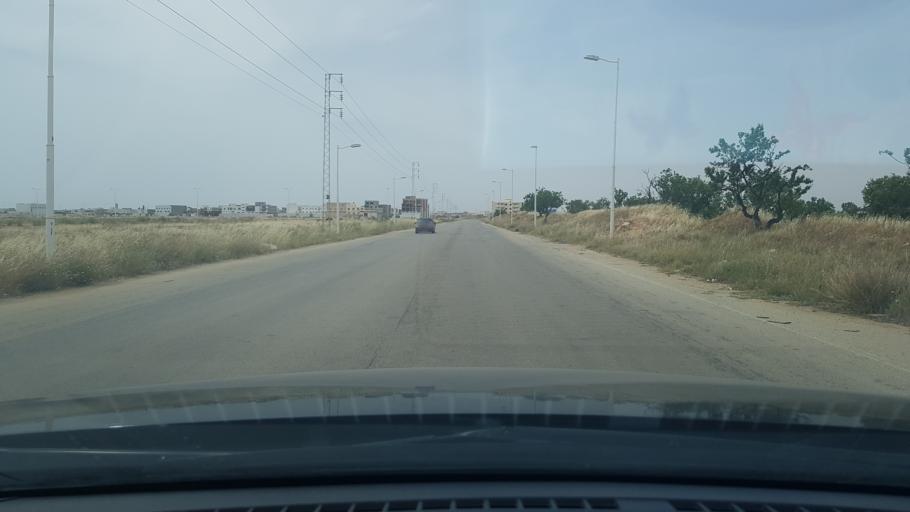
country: TN
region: Safaqis
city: Al Qarmadah
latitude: 34.8323
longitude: 10.7439
